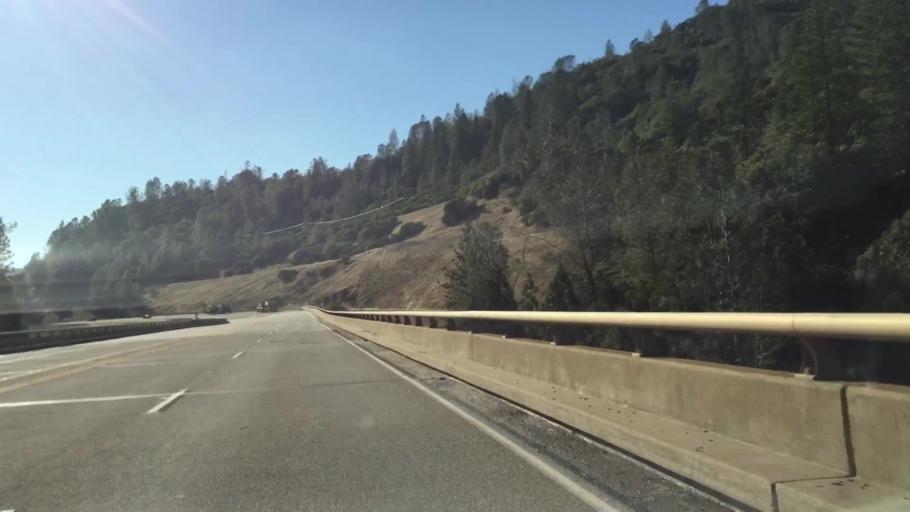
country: US
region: California
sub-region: Butte County
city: Paradise
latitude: 39.6638
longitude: -121.5335
